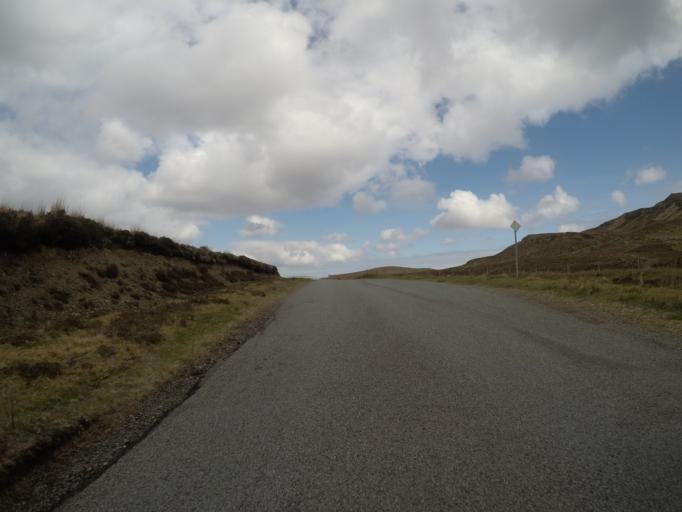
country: GB
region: Scotland
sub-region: Highland
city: Isle of Skye
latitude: 57.3848
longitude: -6.3535
